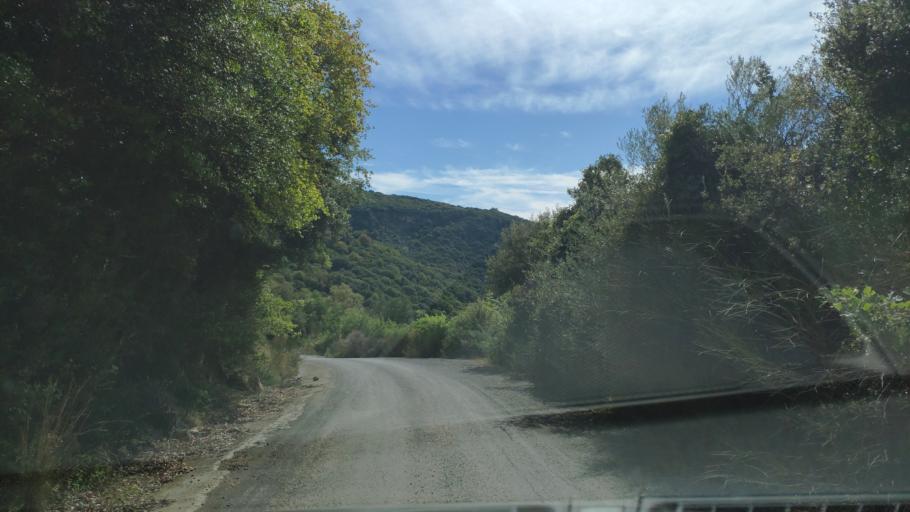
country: GR
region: Peloponnese
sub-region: Nomos Arkadias
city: Dimitsana
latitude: 37.5394
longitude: 22.0501
